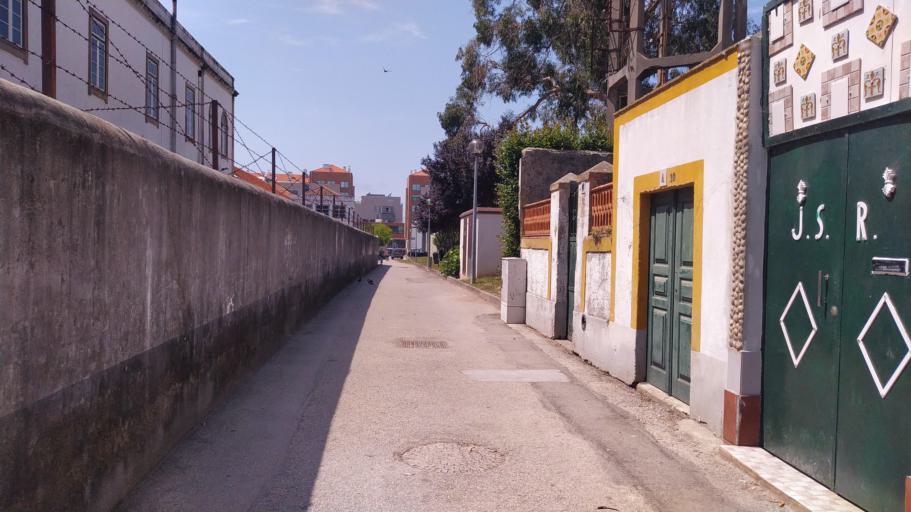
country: PT
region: Aveiro
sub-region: Aveiro
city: Aveiro
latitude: 40.6461
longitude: -8.6455
